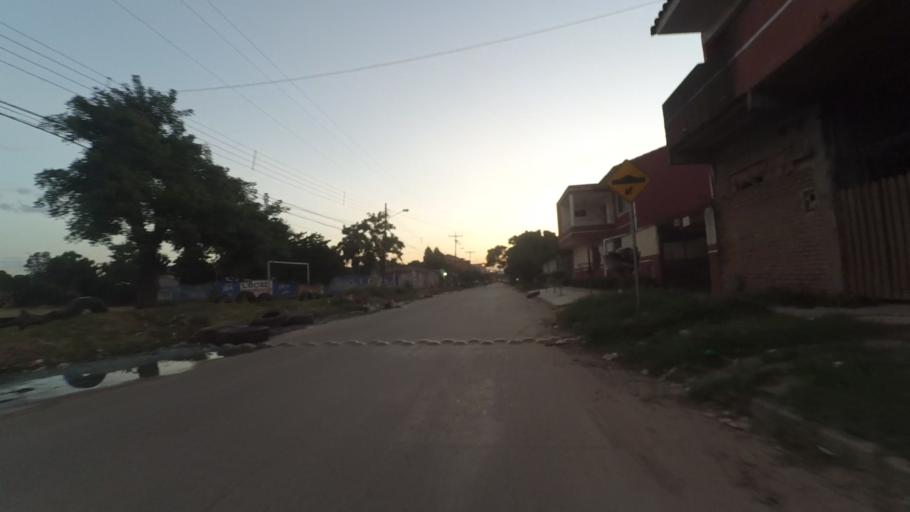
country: BO
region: Santa Cruz
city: Santa Cruz de la Sierra
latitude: -17.8208
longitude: -63.1330
